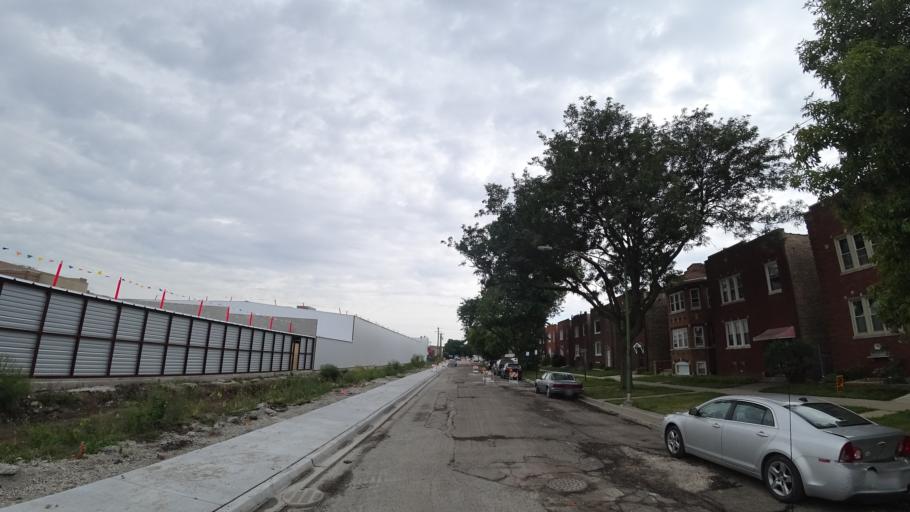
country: US
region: Illinois
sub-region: Cook County
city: Oak Park
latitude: 41.8670
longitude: -87.7692
